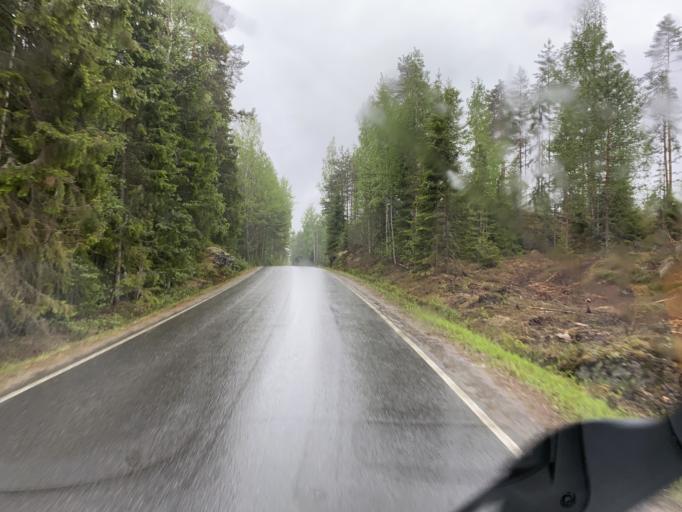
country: FI
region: Haeme
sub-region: Forssa
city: Humppila
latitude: 61.0868
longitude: 23.3093
